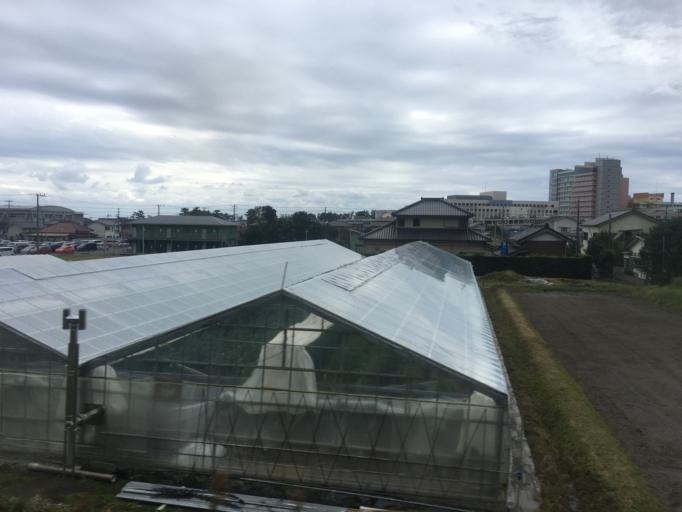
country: JP
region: Chiba
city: Kawaguchi
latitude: 35.1245
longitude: 140.1288
